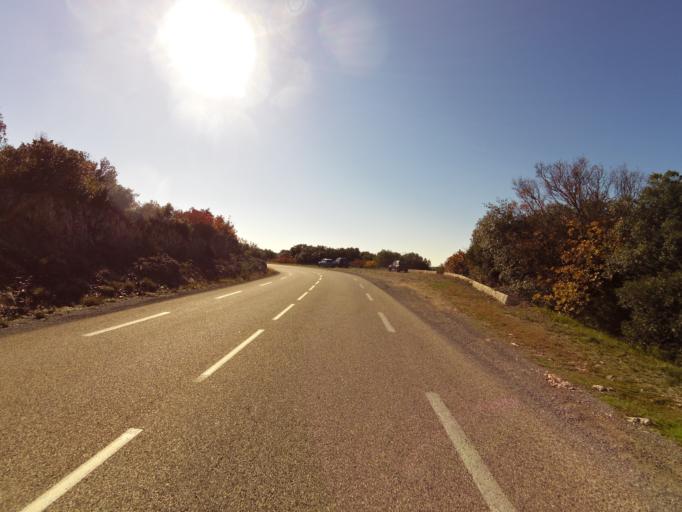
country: FR
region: Rhone-Alpes
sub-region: Departement de l'Ardeche
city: Ruoms
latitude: 44.4071
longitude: 4.4224
